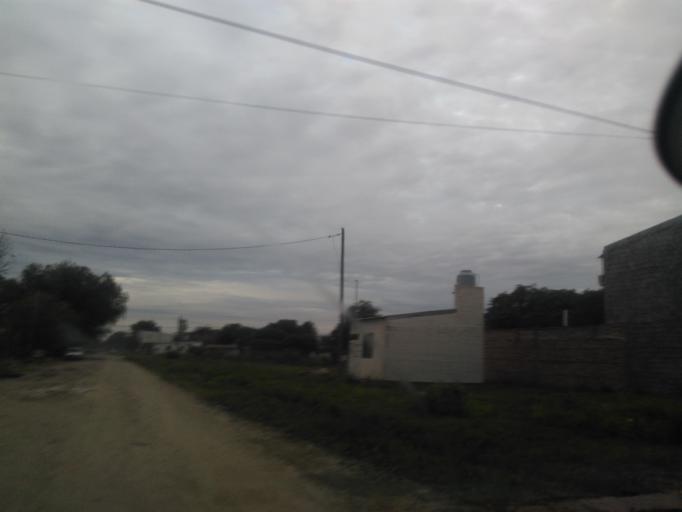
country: AR
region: Chaco
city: Resistencia
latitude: -27.4719
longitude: -59.0114
